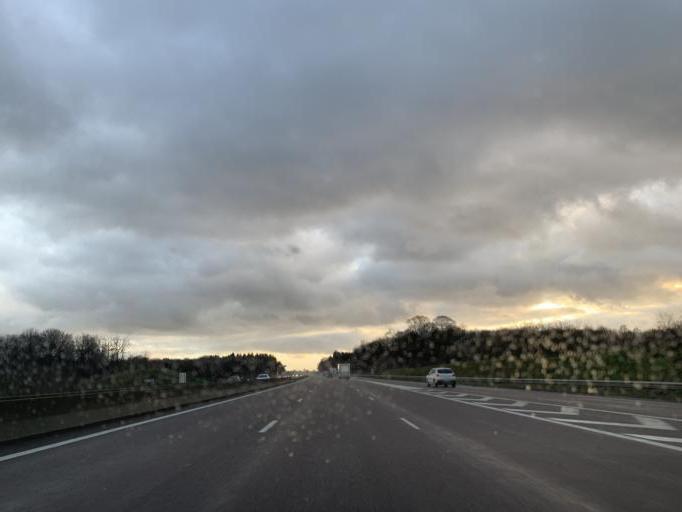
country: FR
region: Champagne-Ardenne
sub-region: Departement de la Haute-Marne
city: Langres
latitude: 47.8124
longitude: 5.2236
